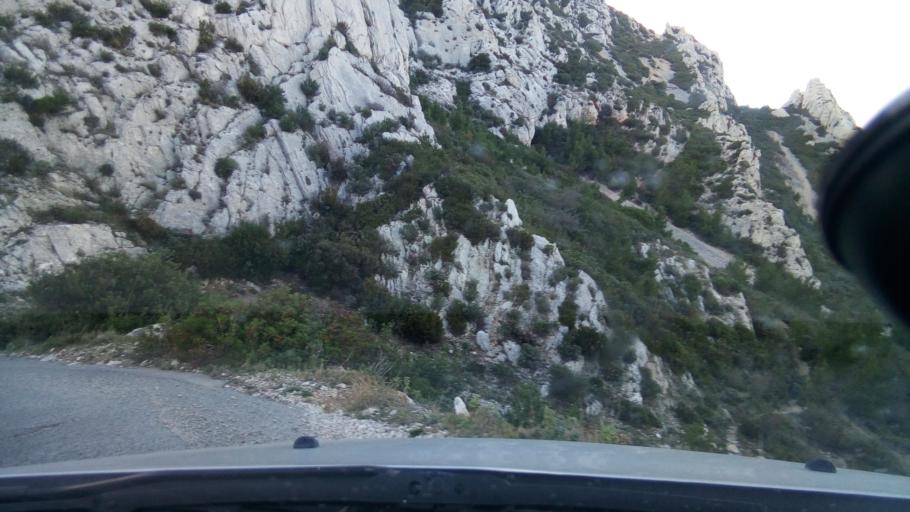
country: FR
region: Provence-Alpes-Cote d'Azur
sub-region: Departement des Bouches-du-Rhone
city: Marseille 09
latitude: 43.2175
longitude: 5.4074
